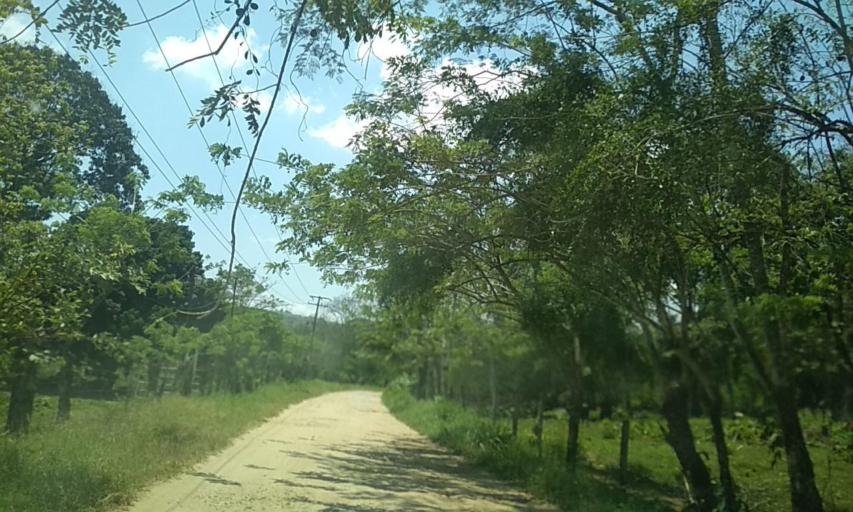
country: MX
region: Chiapas
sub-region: Tecpatan
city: Raudales Malpaso
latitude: 17.2839
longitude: -93.8348
